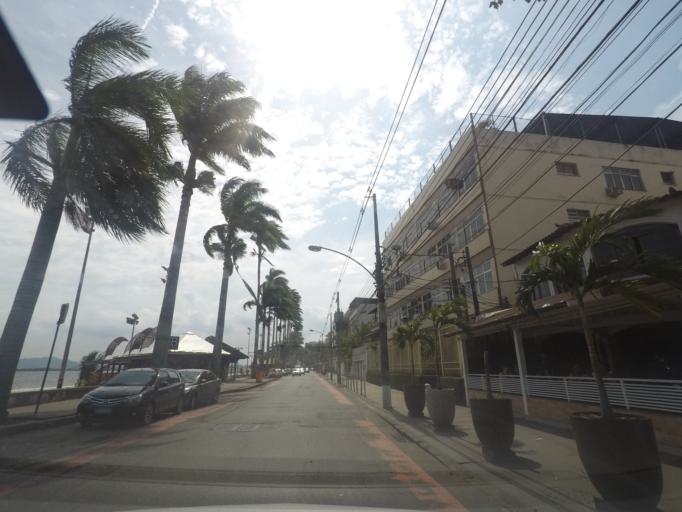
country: BR
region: Rio de Janeiro
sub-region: Rio De Janeiro
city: Rio de Janeiro
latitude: -22.8185
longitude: -43.1974
